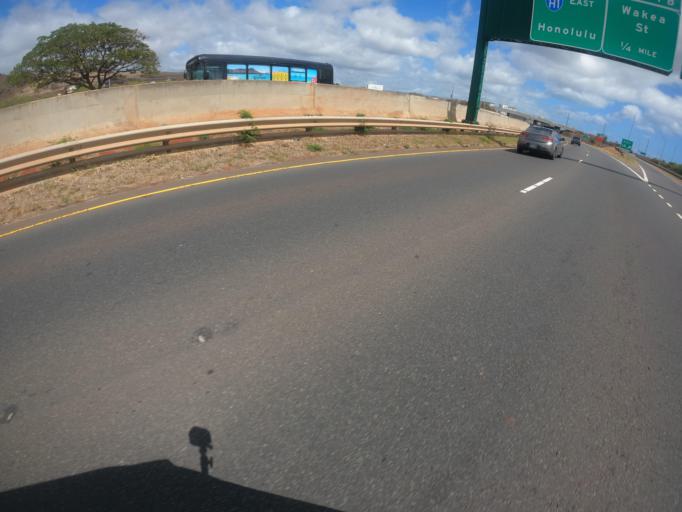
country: US
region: Hawaii
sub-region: Honolulu County
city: Makakilo City
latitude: 21.3326
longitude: -158.0917
